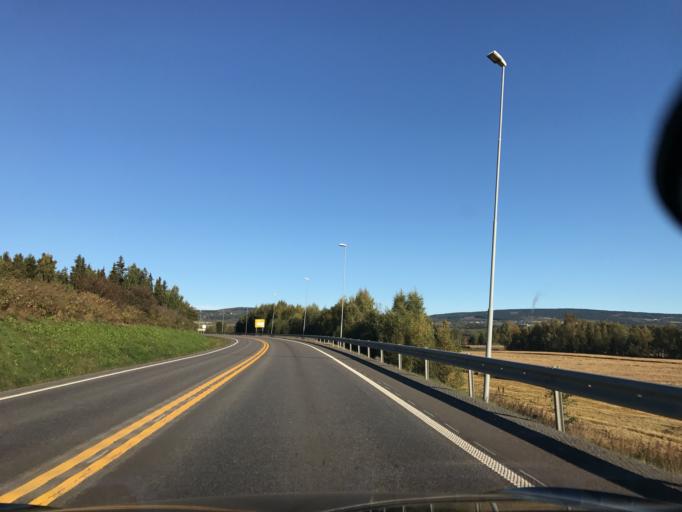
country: NO
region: Hedmark
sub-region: Hamar
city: Hamar
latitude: 60.8265
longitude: 11.0892
